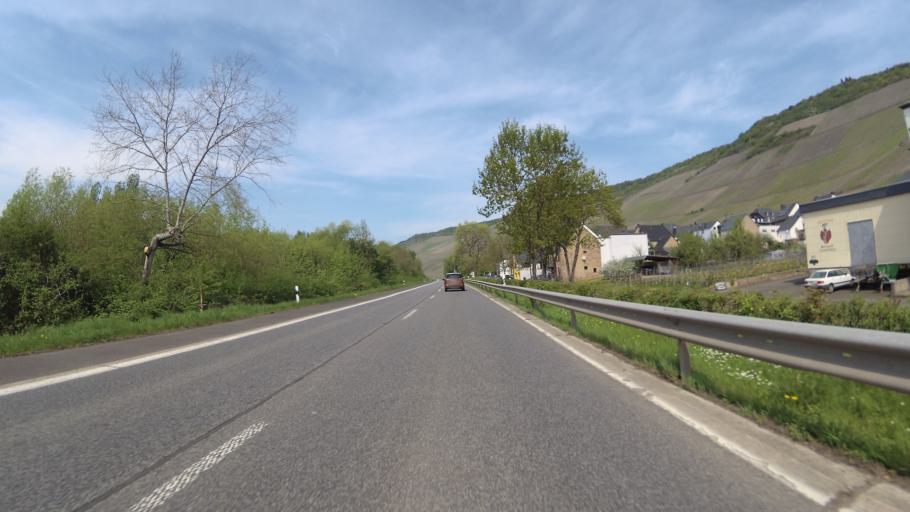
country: DE
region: Rheinland-Pfalz
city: Bernkastel-Kues
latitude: 49.9367
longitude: 7.0594
